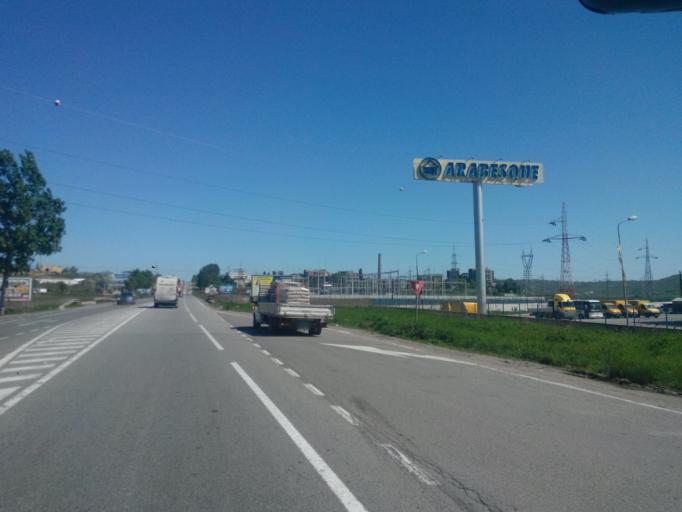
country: RO
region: Iasi
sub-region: Comuna Valea Lupului
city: Valea Lupului
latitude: 47.1803
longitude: 27.4754
